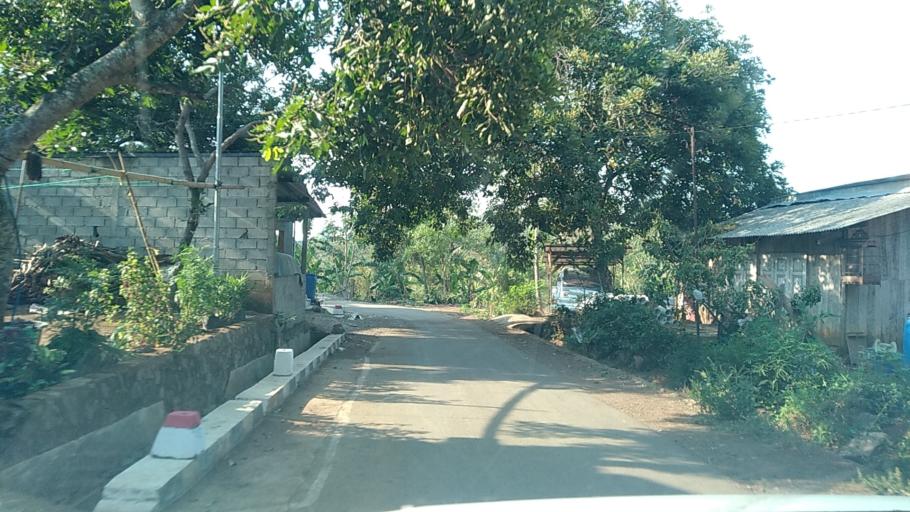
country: ID
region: Central Java
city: Ungaran
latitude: -7.0699
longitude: 110.3537
